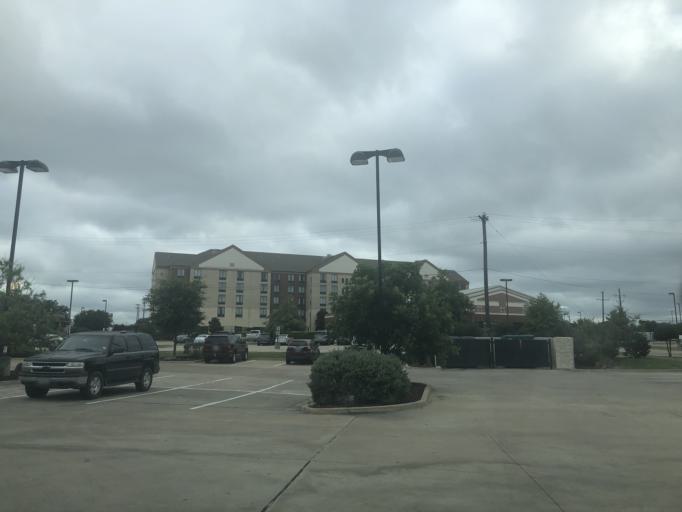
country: US
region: Texas
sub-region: Dallas County
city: Duncanville
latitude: 32.6621
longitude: -96.9054
